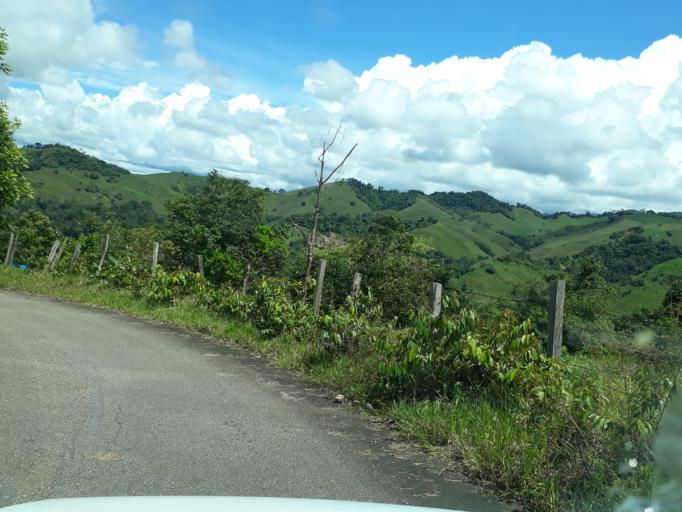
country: CO
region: Cundinamarca
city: Medina
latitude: 4.5779
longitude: -73.3231
